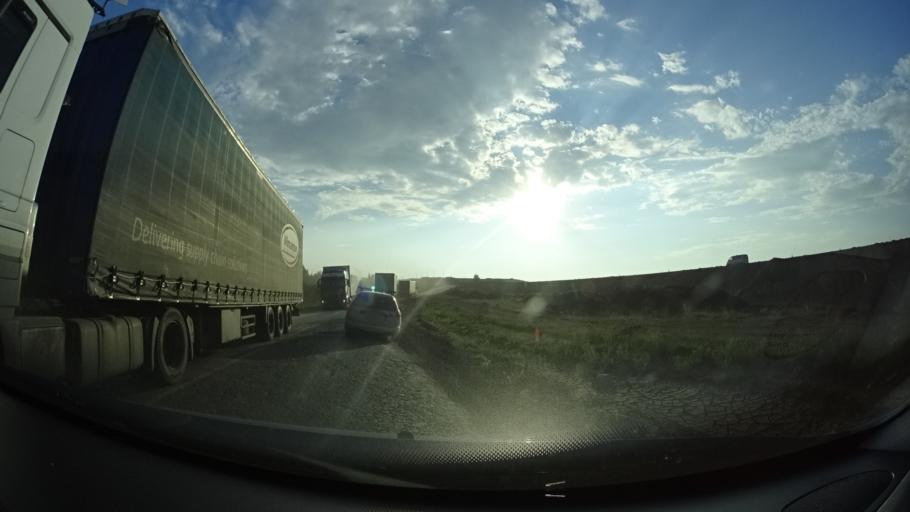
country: RU
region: Samara
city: Kamyshla
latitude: 54.0680
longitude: 52.1682
